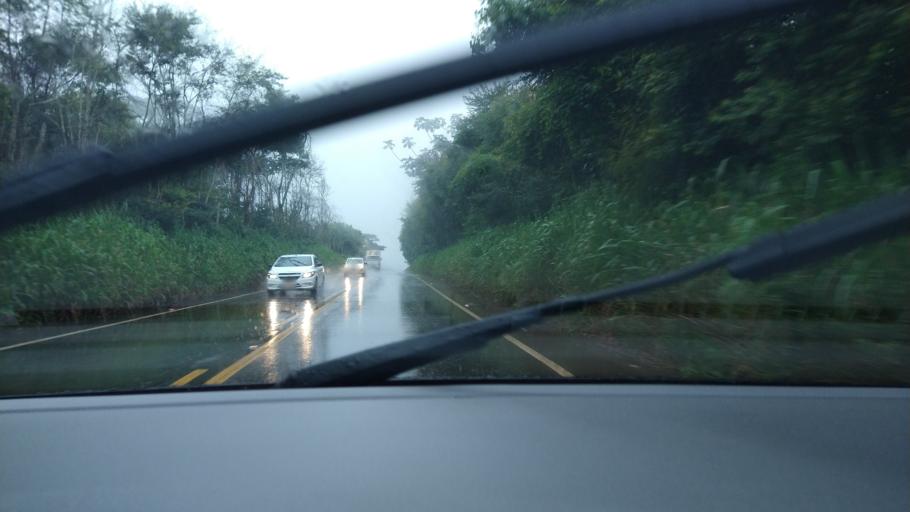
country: BR
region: Minas Gerais
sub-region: Ponte Nova
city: Ponte Nova
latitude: -20.5643
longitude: -42.8724
